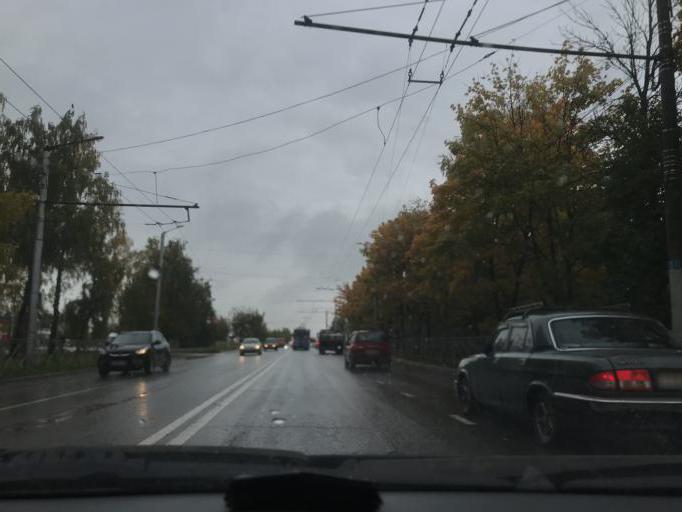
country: RU
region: Kaluga
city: Kaluga
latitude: 54.5401
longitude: 36.3148
